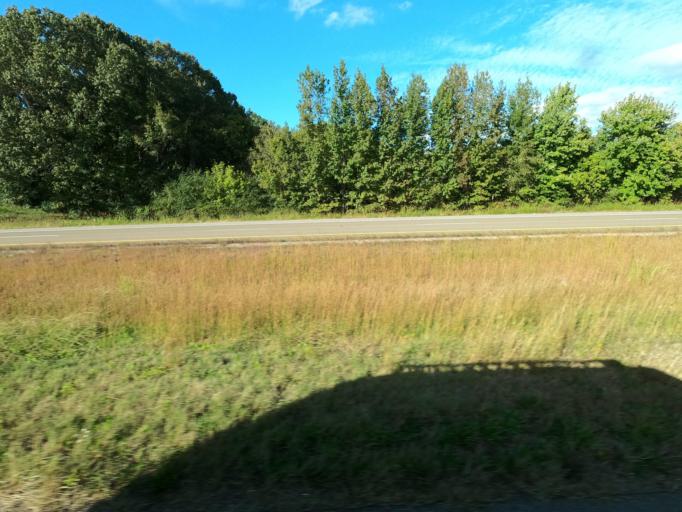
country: US
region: Tennessee
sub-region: Madison County
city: Jackson
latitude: 35.6678
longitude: -88.9079
